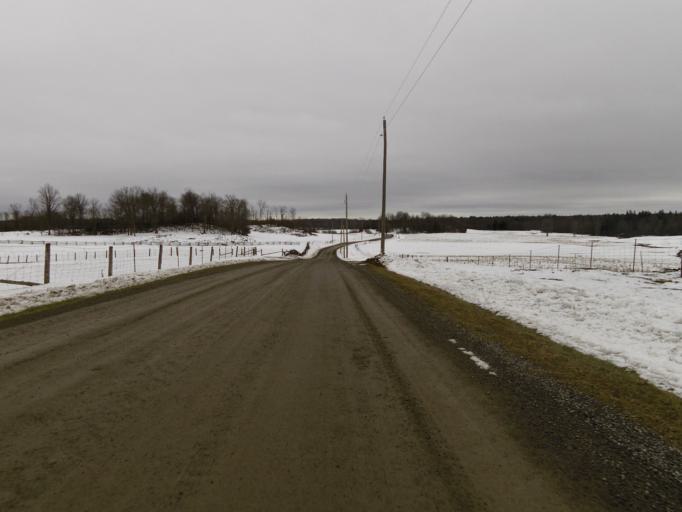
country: CA
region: Ontario
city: Carleton Place
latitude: 45.2050
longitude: -76.2126
